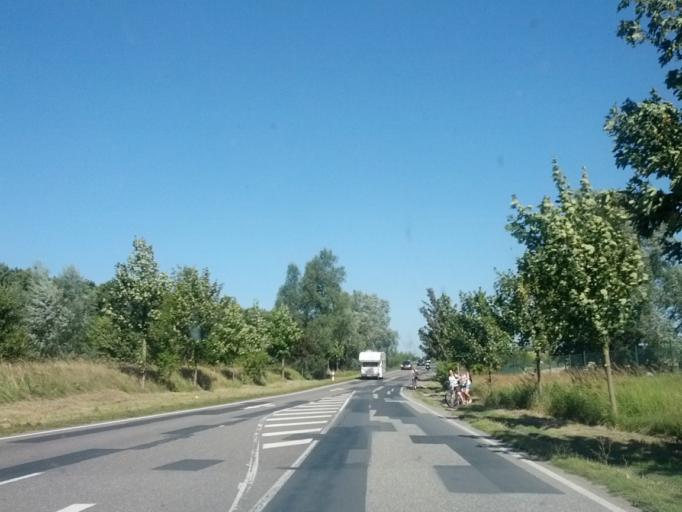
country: DE
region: Mecklenburg-Vorpommern
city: Sagard
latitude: 54.4844
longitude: 13.5776
